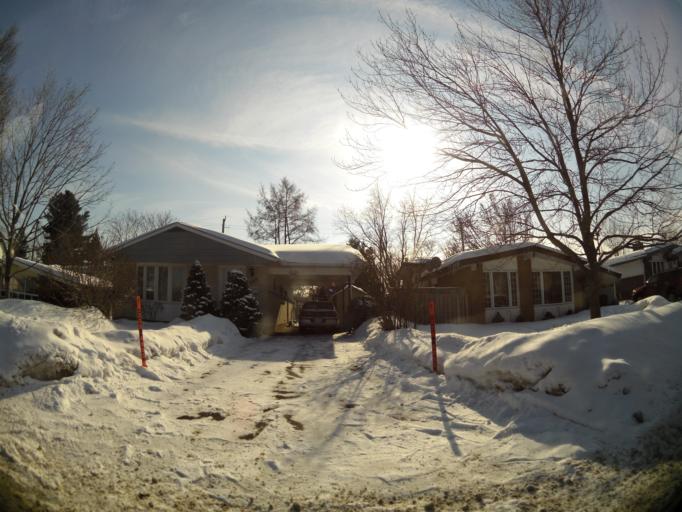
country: CA
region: Ontario
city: Ottawa
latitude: 45.3836
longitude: -75.6375
